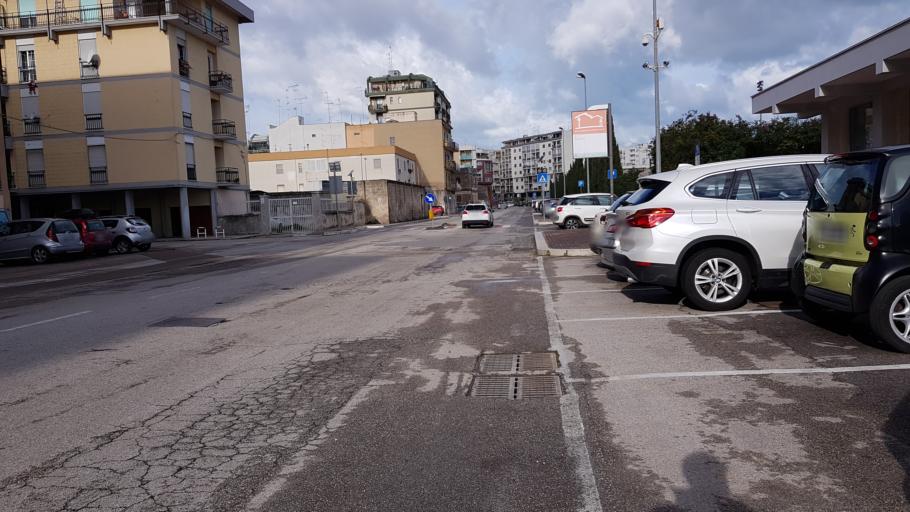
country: IT
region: Apulia
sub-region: Provincia di Brindisi
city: Brindisi
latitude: 40.6337
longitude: 17.9384
